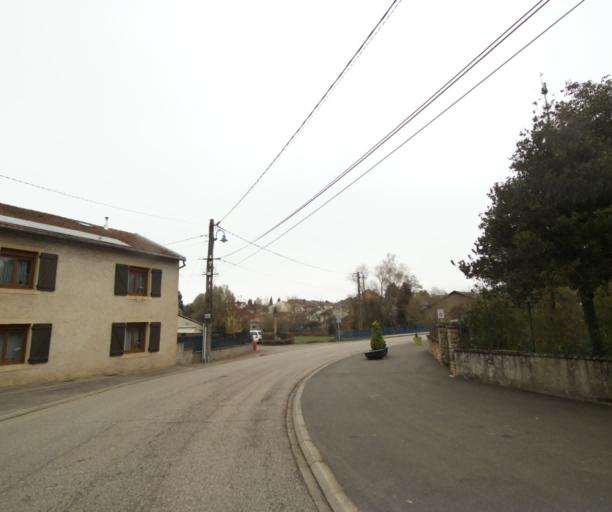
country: FR
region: Lorraine
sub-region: Departement de Meurthe-et-Moselle
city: Mancieulles
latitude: 49.2668
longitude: 5.9140
